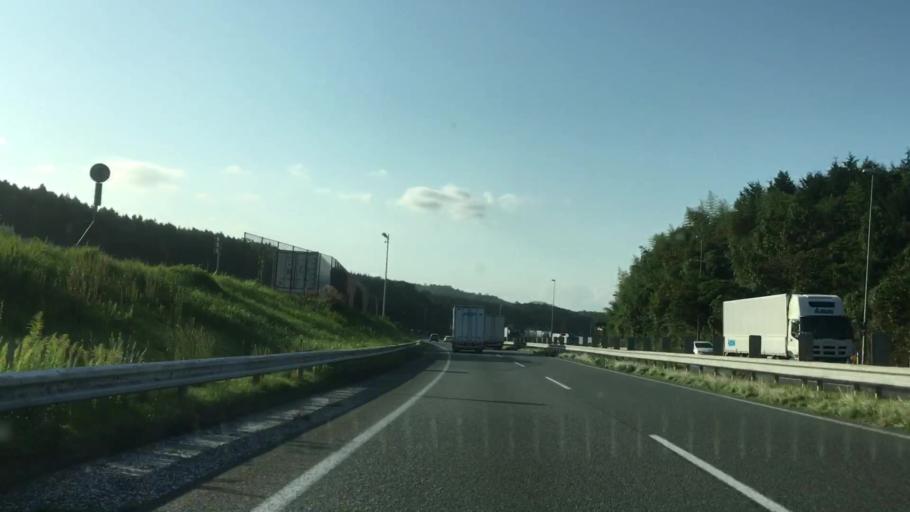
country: JP
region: Yamaguchi
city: Ogori-shimogo
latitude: 34.1527
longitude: 131.3395
